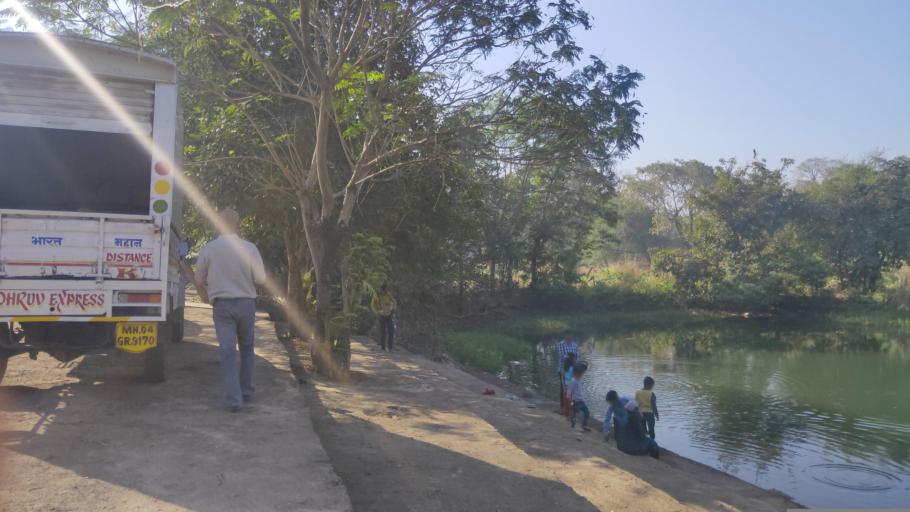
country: IN
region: Maharashtra
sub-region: Thane
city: Bhiwandi
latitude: 19.3008
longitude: 73.0142
